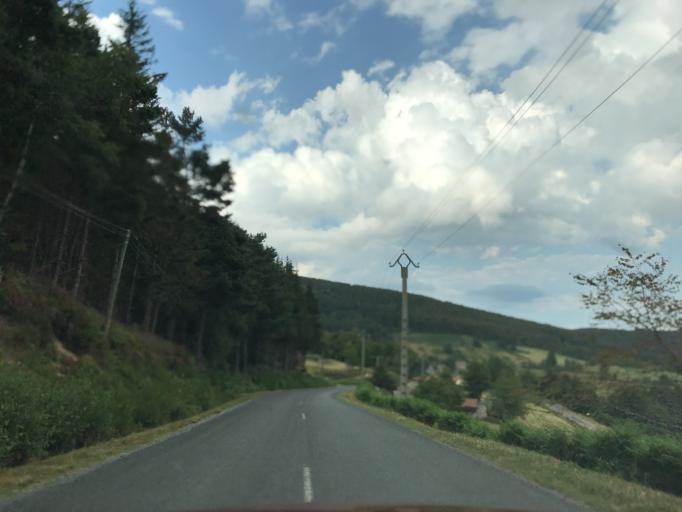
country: FR
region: Rhone-Alpes
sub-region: Departement de la Loire
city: Noiretable
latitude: 45.7554
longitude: 3.7414
